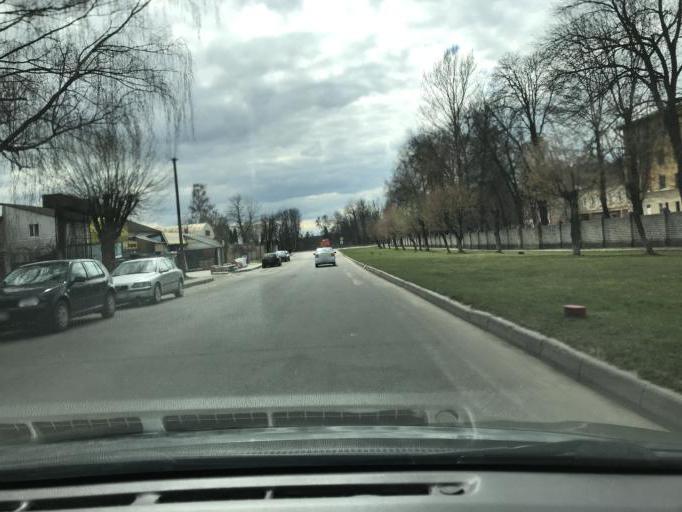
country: BY
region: Mogilev
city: Mahilyow
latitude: 53.9239
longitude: 30.3596
